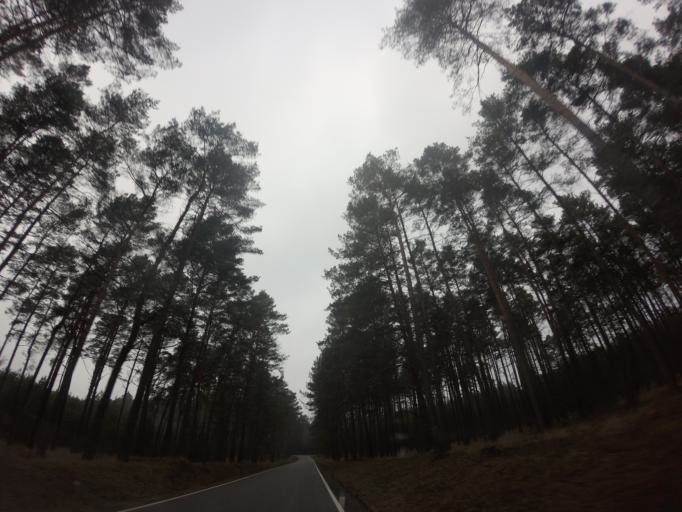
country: PL
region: West Pomeranian Voivodeship
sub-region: Powiat choszczenski
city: Drawno
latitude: 53.1237
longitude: 15.7339
